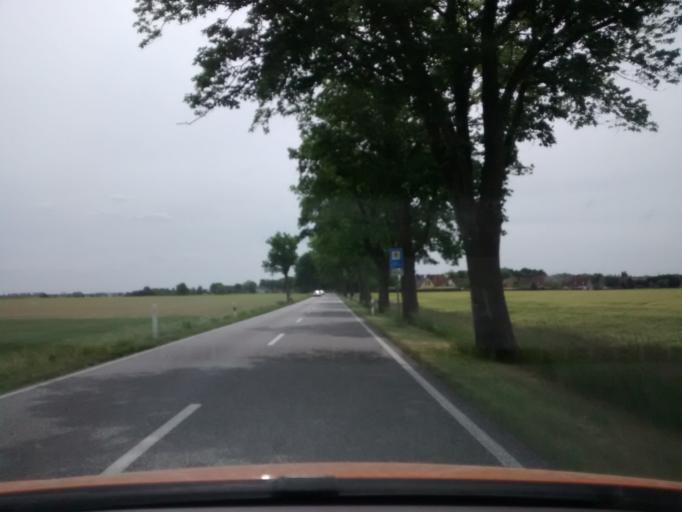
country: DE
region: Brandenburg
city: Juterbog
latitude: 51.9371
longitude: 13.1204
